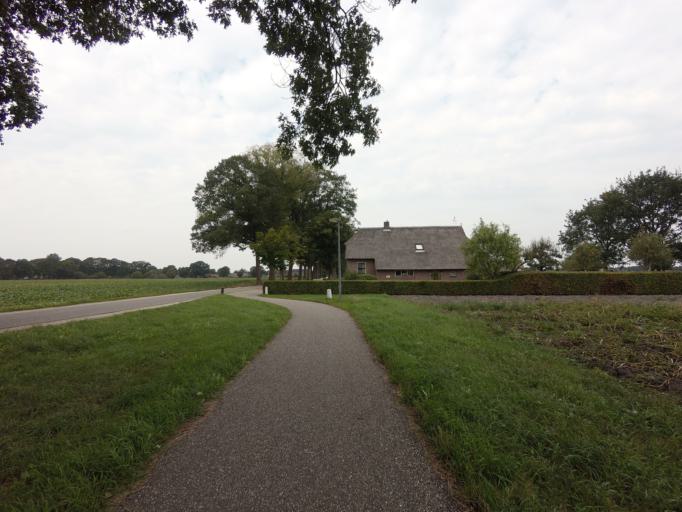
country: NL
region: Drenthe
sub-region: Gemeente Assen
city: Assen
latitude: 52.9924
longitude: 6.6381
